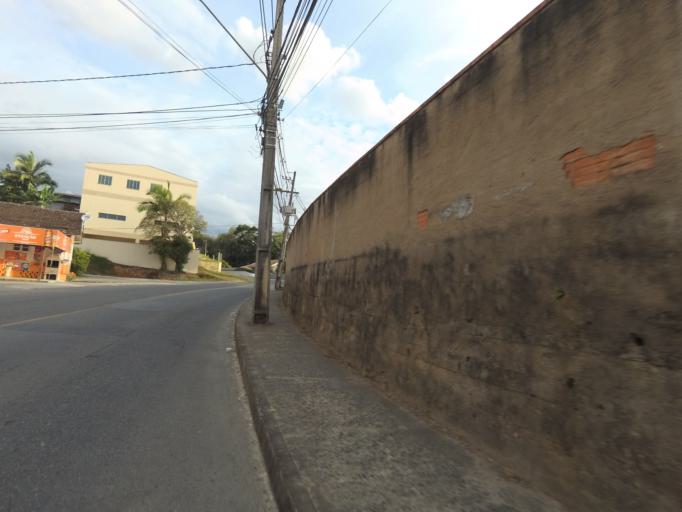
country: BR
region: Santa Catarina
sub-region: Blumenau
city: Blumenau
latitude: -26.9062
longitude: -49.1231
